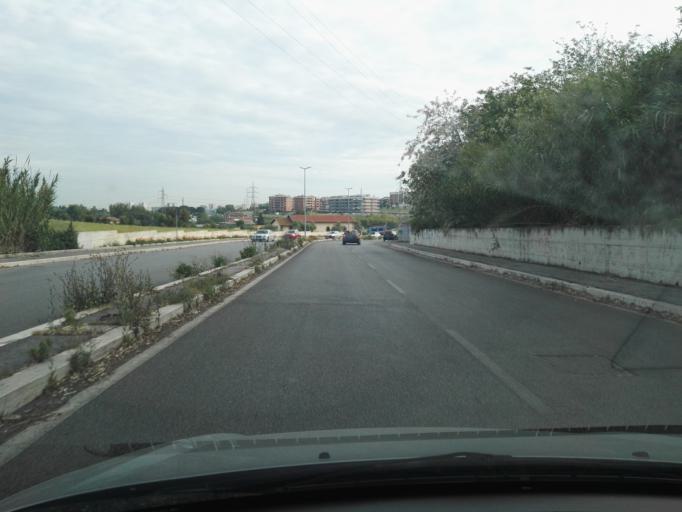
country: IT
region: Latium
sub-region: Citta metropolitana di Roma Capitale
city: Selcetta
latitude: 41.7863
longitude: 12.4806
